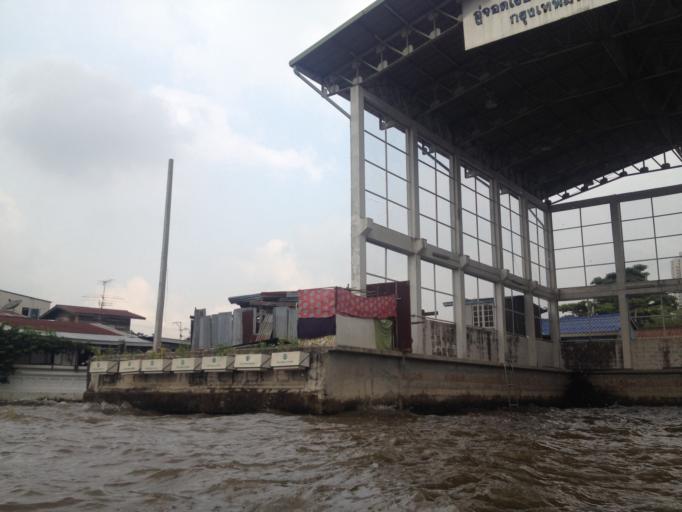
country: TH
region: Bangkok
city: Bangkok Noi
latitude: 13.7621
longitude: 100.4806
